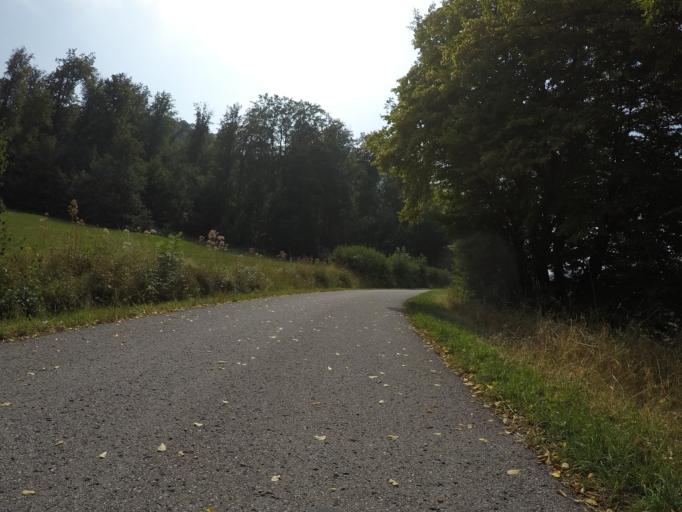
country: DE
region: Baden-Wuerttemberg
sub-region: Tuebingen Region
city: Pfullingen
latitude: 48.4421
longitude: 9.2032
